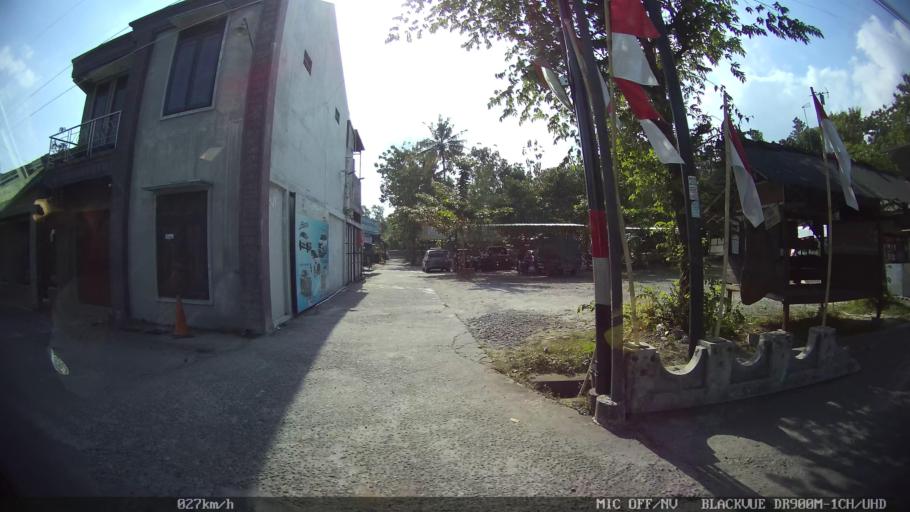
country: ID
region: Daerah Istimewa Yogyakarta
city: Kasihan
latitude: -7.8393
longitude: 110.3346
